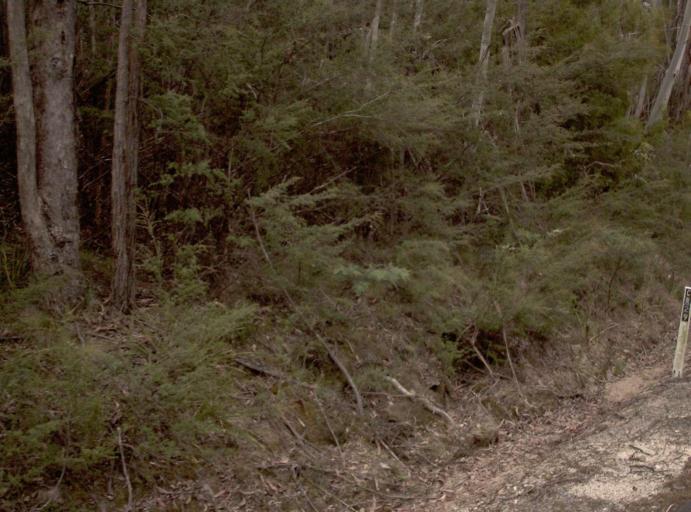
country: AU
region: New South Wales
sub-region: Bombala
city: Bombala
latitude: -37.3399
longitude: 149.2064
